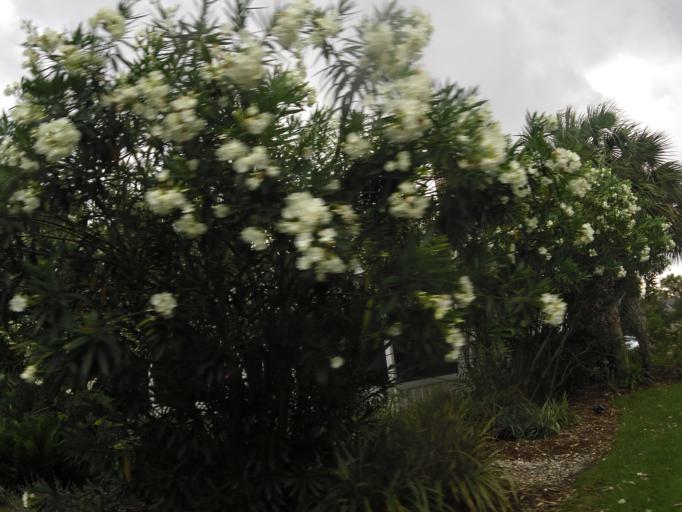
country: US
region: Florida
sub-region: Saint Johns County
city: Ponte Vedra Beach
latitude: 30.2625
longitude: -81.3905
